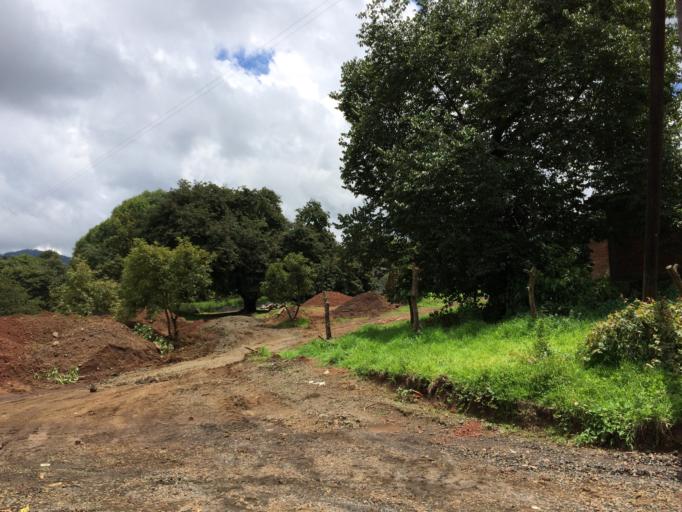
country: MX
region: Michoacan
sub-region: Uruapan
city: Nuevo Zirosto
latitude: 19.5472
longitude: -102.3434
